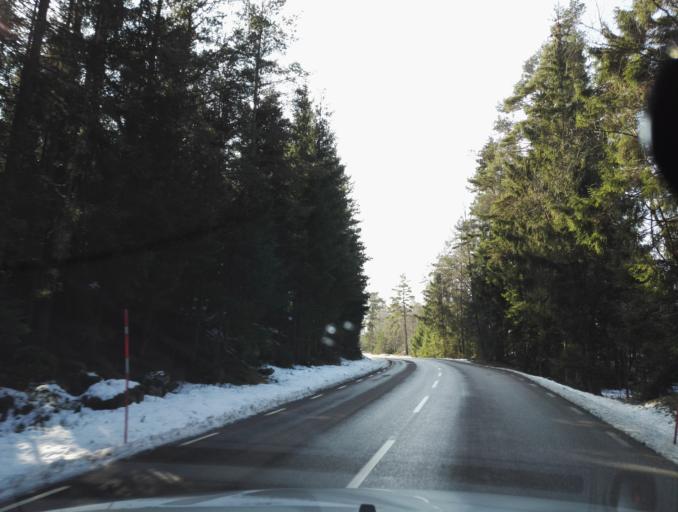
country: SE
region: Vaestra Goetaland
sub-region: Bollebygds Kommun
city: Bollebygd
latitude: 57.7126
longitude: 12.5822
